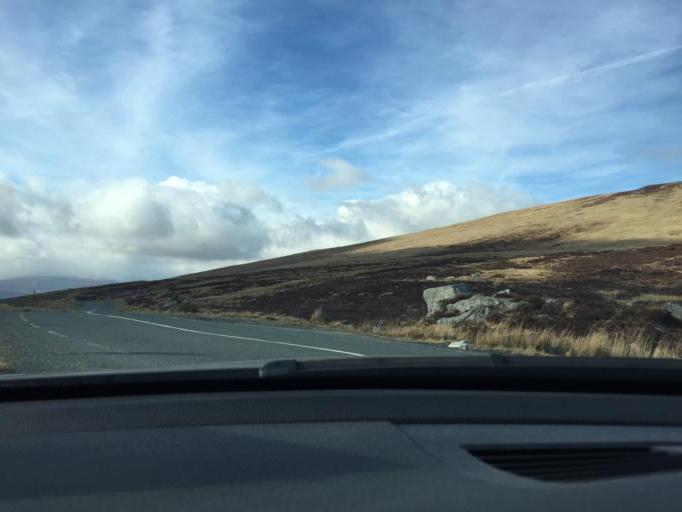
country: IE
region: Leinster
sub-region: Wicklow
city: Valleymount
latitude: 53.0418
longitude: -6.3979
